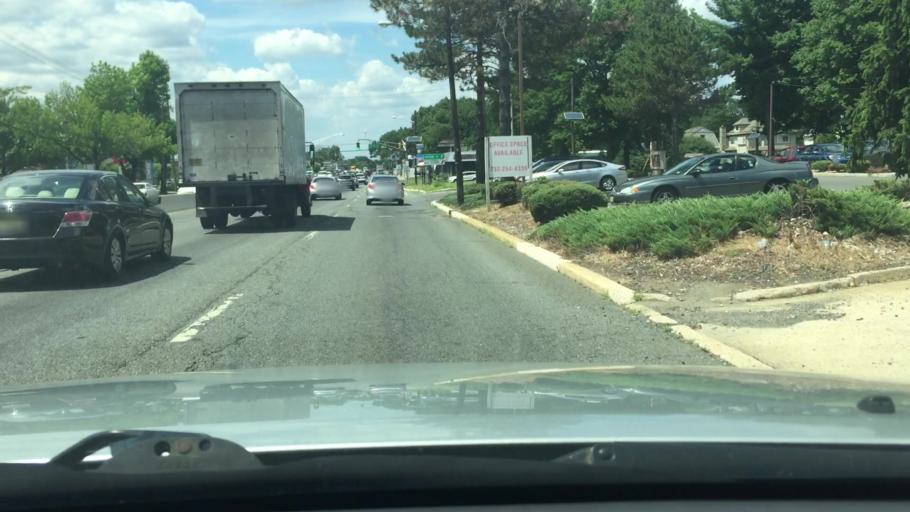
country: US
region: New Jersey
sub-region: Middlesex County
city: South River
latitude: 40.4332
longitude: -74.3877
